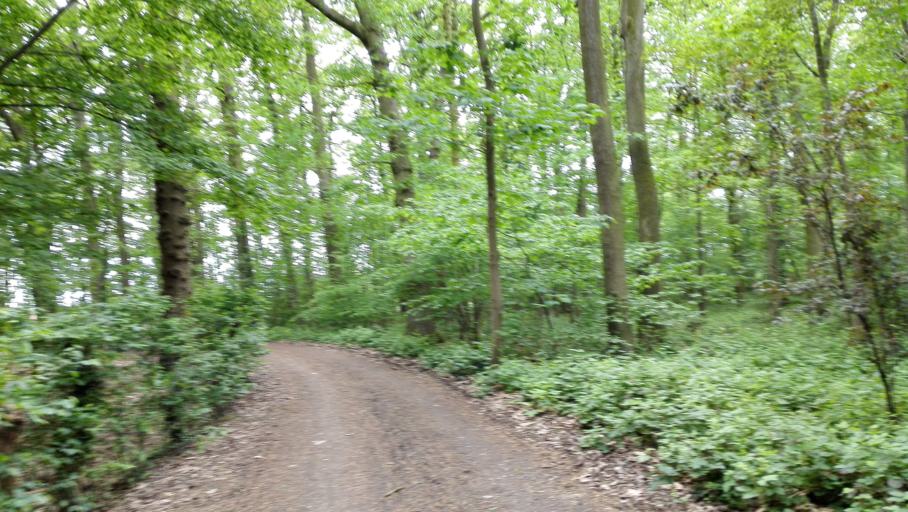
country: BE
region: Flanders
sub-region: Provincie Vlaams-Brabant
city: Holsbeek
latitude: 50.8932
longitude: 4.7563
